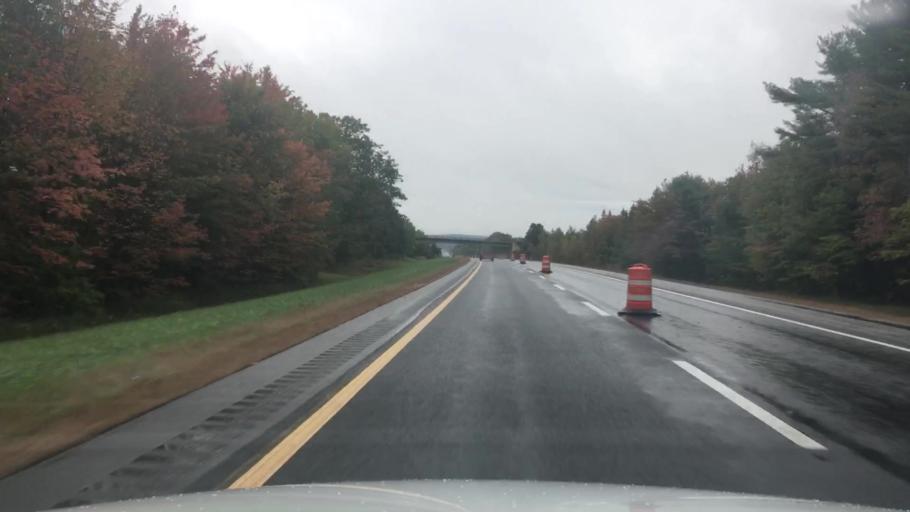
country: US
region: Maine
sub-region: Sagadahoc County
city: Richmond
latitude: 44.1254
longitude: -69.8483
